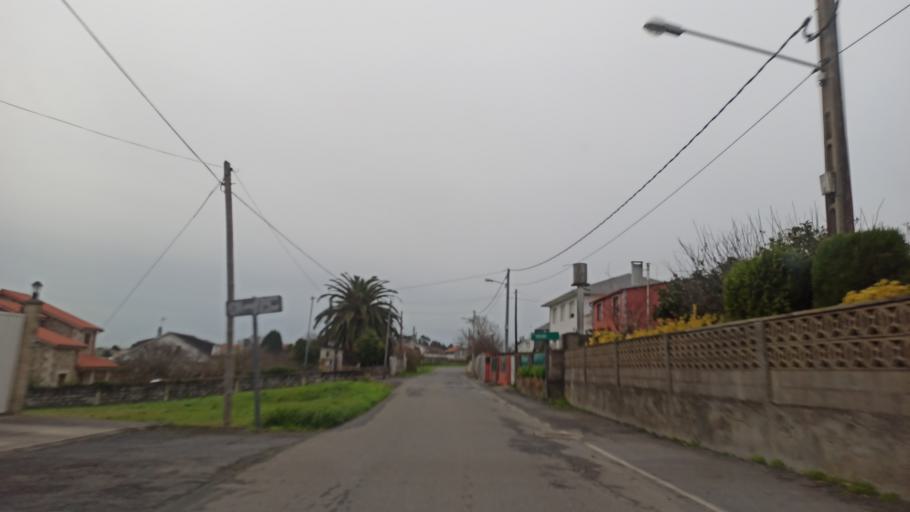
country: ES
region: Galicia
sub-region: Provincia da Coruna
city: Oleiros
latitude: 43.3953
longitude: -8.3185
